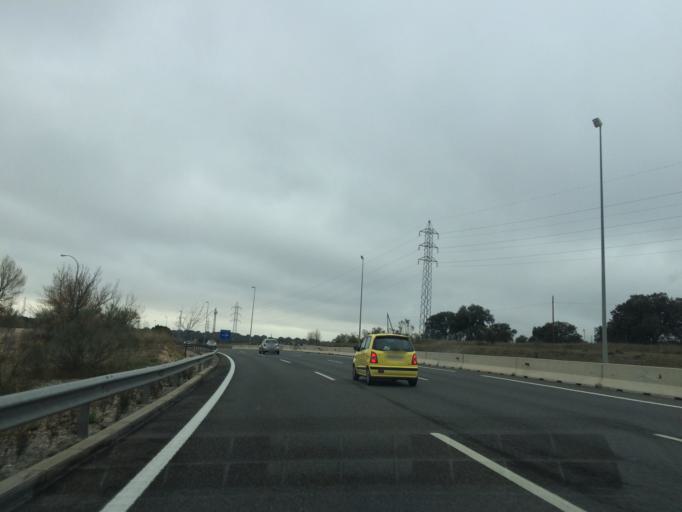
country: ES
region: Madrid
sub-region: Provincia de Madrid
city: Tres Cantos
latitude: 40.5649
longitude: -3.7141
